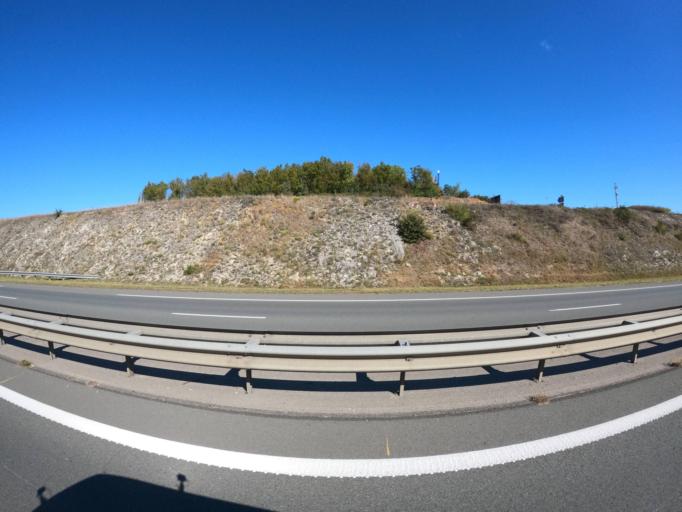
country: FR
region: Poitou-Charentes
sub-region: Departement de la Vienne
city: Migne-Auxances
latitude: 46.6201
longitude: 0.3421
